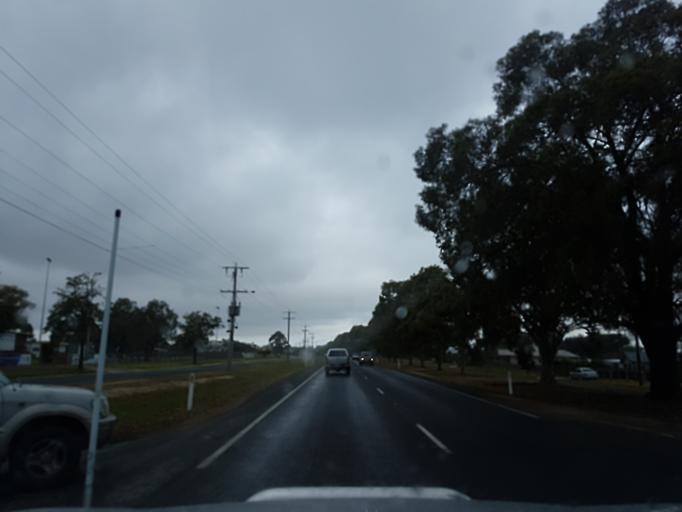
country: AU
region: Victoria
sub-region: East Gippsland
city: Bairnsdale
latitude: -37.8123
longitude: 147.6474
